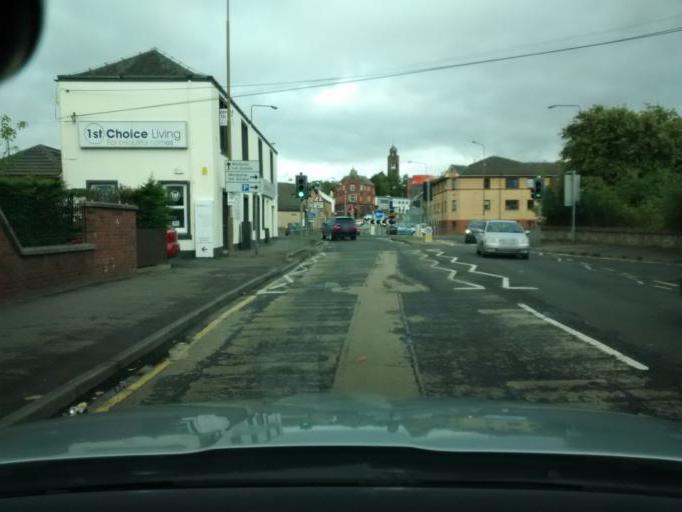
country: GB
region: Scotland
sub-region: West Lothian
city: Bathgate
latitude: 55.9018
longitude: -3.6477
